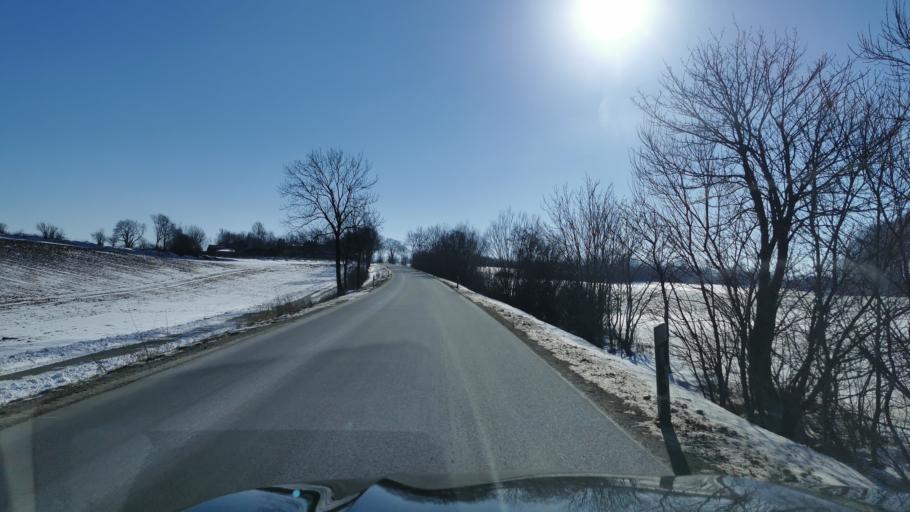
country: DE
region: Schleswig-Holstein
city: Grundhof
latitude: 54.7850
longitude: 9.6442
